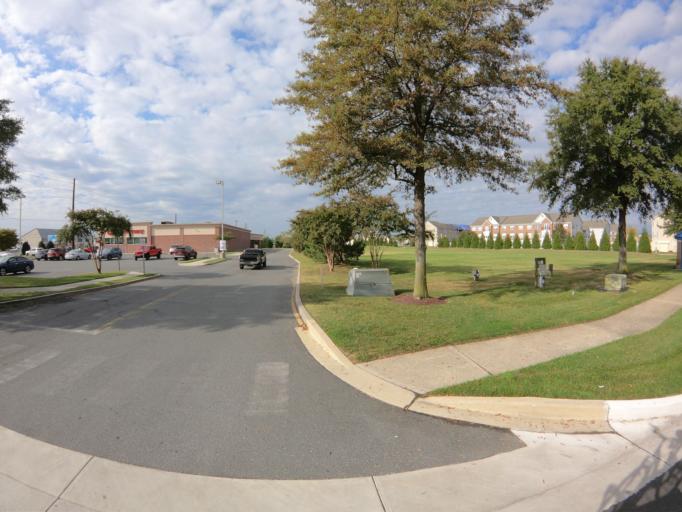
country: US
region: Delaware
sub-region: Sussex County
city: Lewes
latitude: 38.7513
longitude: -75.1683
